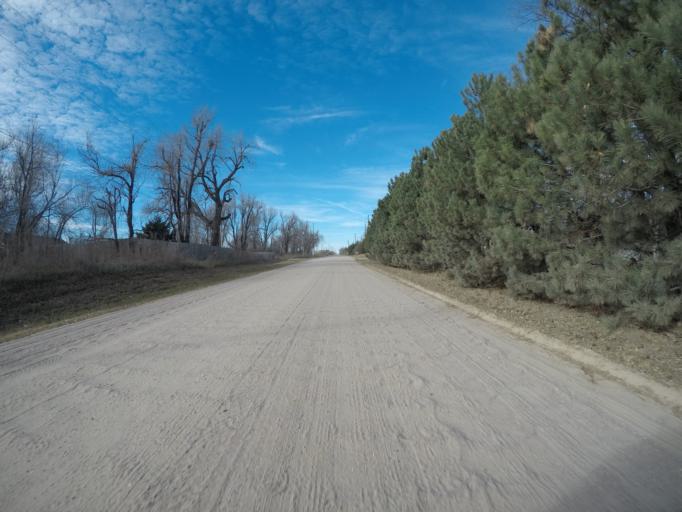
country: US
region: Kansas
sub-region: Reno County
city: Hutchinson
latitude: 38.1011
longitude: -97.8646
